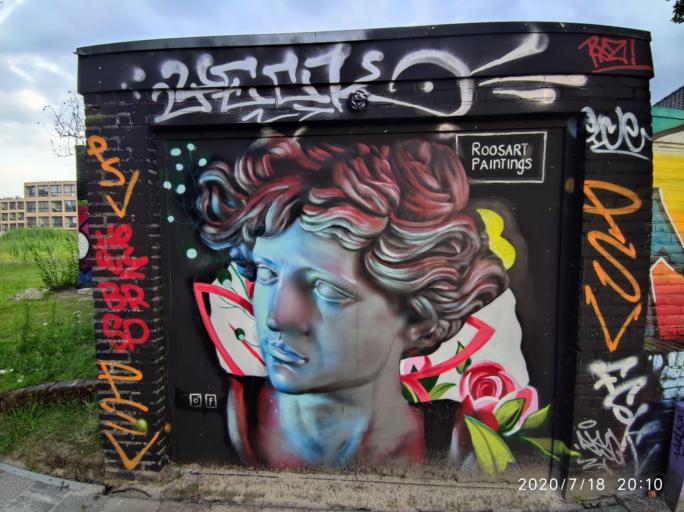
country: NL
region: North Brabant
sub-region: Gemeente Eindhoven
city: Lakerlopen
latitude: 51.4468
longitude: 5.5016
